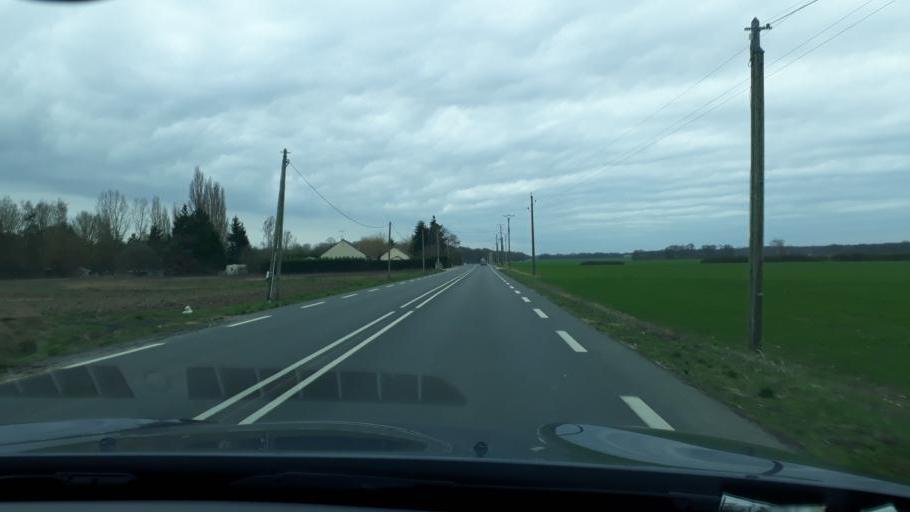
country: FR
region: Centre
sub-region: Departement du Loiret
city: Chanteau
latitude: 48.0315
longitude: 1.9739
